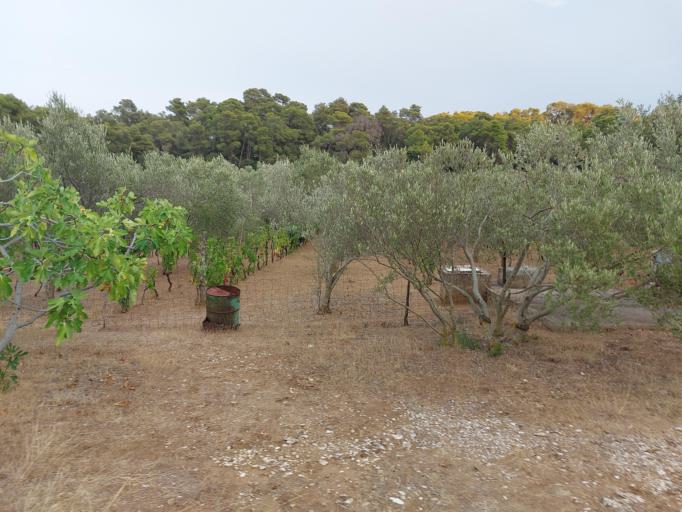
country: HR
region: Dubrovacko-Neretvanska
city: Smokvica
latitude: 42.7606
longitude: 16.9343
